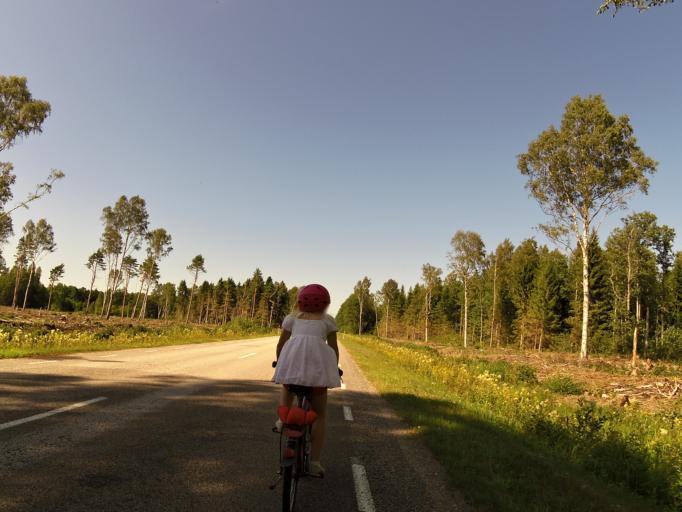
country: EE
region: Hiiumaa
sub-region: Kaerdla linn
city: Kardla
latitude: 58.8438
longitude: 22.4674
